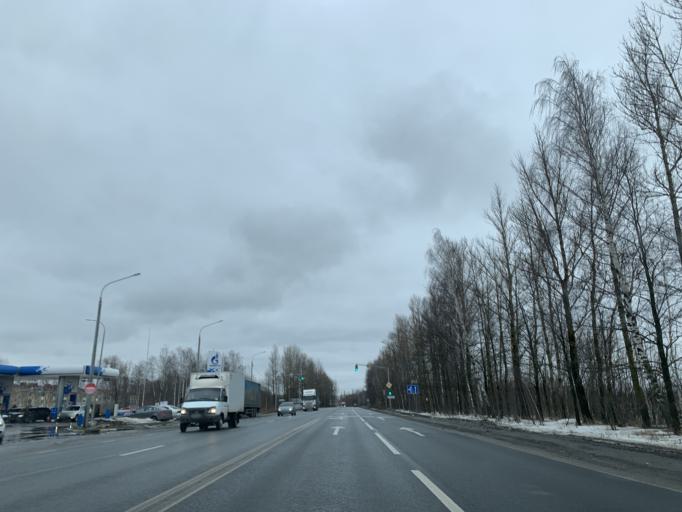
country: RU
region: Jaroslavl
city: Yaroslavl
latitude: 57.7242
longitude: 39.7488
